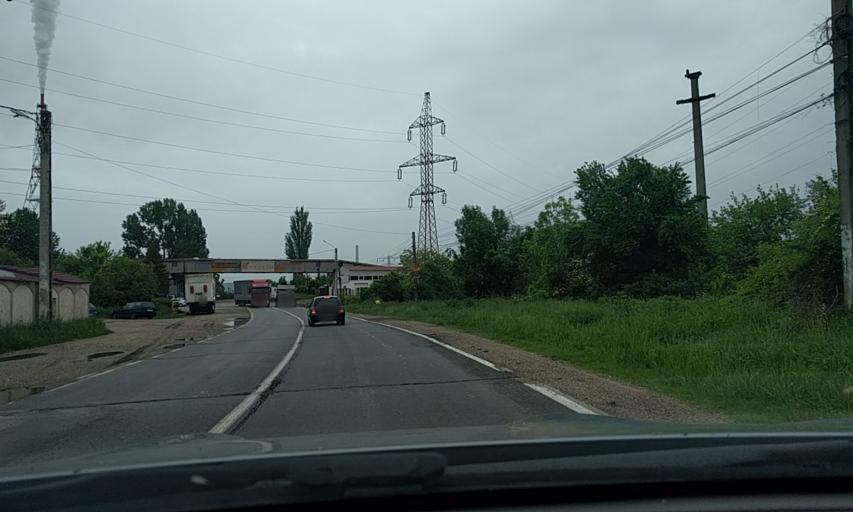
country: RO
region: Dambovita
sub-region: Comuna Aninoasa
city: Sateni
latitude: 44.9843
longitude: 25.4182
